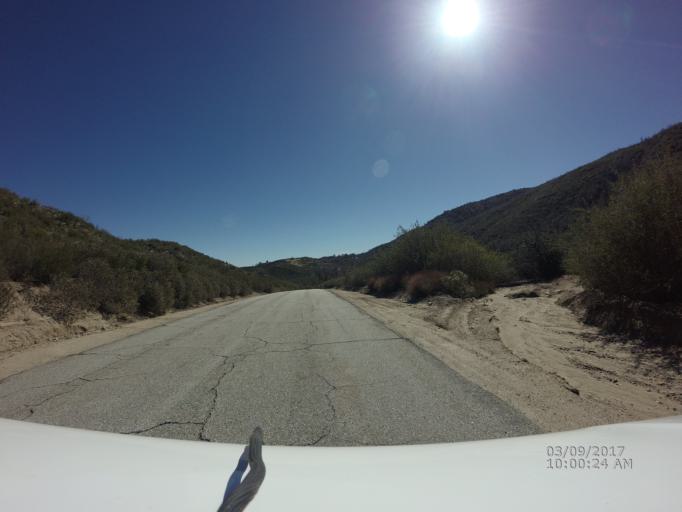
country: US
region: California
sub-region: Kern County
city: Lebec
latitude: 34.7385
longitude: -118.6528
